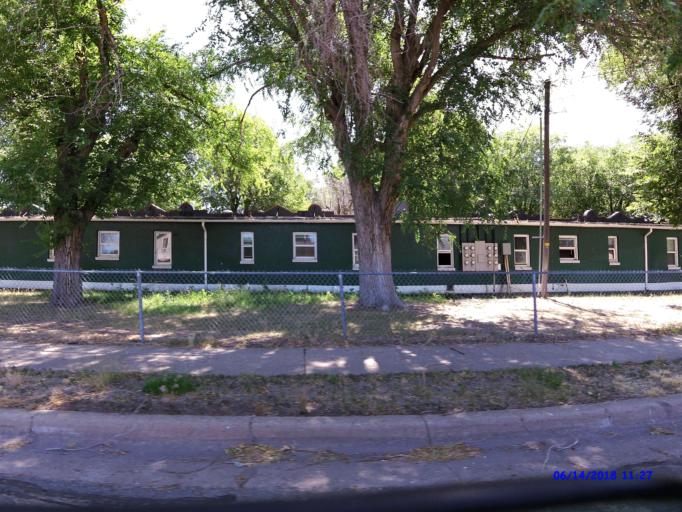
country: US
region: Utah
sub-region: Weber County
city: Ogden
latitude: 41.2226
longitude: -111.9927
